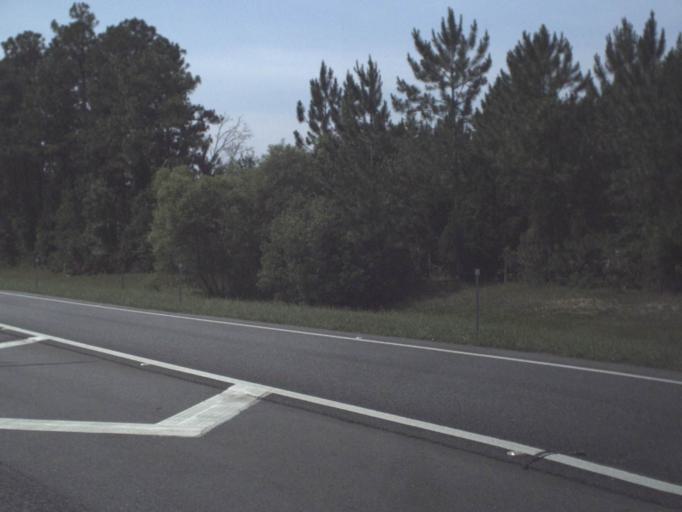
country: US
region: Florida
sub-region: Nassau County
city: Yulee
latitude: 30.6225
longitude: -81.6512
